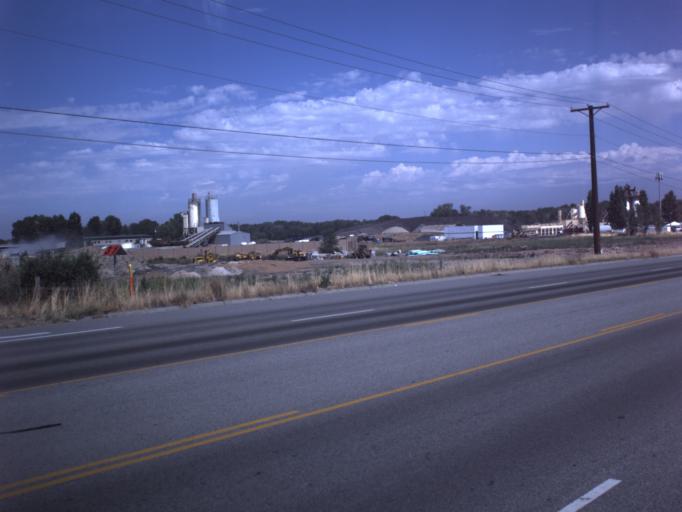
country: US
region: Utah
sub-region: Weber County
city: Marriott-Slaterville
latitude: 41.2339
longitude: -112.0254
